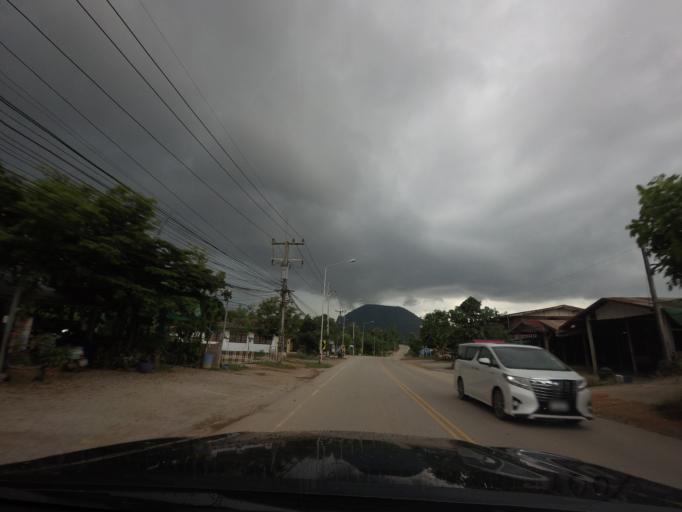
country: LA
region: Vientiane
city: Muang Sanakham
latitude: 17.9465
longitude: 101.7393
